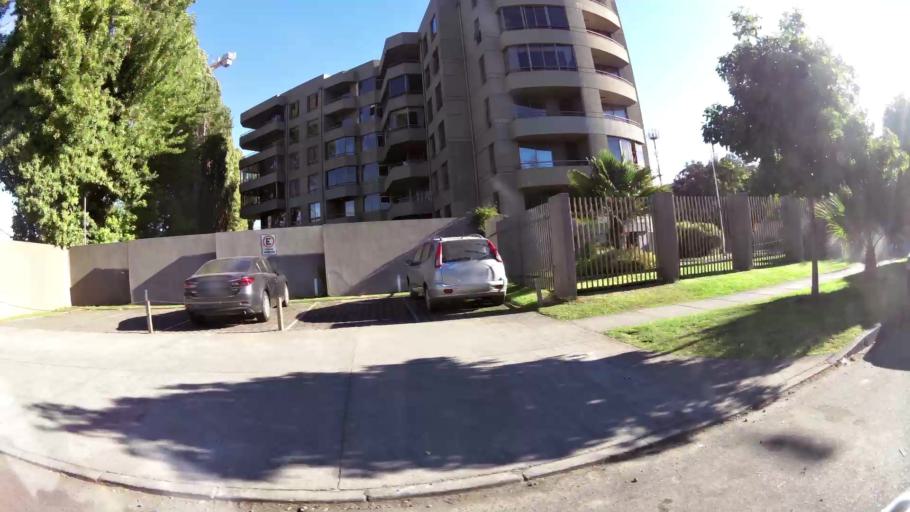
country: CL
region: Biobio
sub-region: Provincia de Concepcion
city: Concepcion
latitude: -36.8370
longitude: -73.1037
